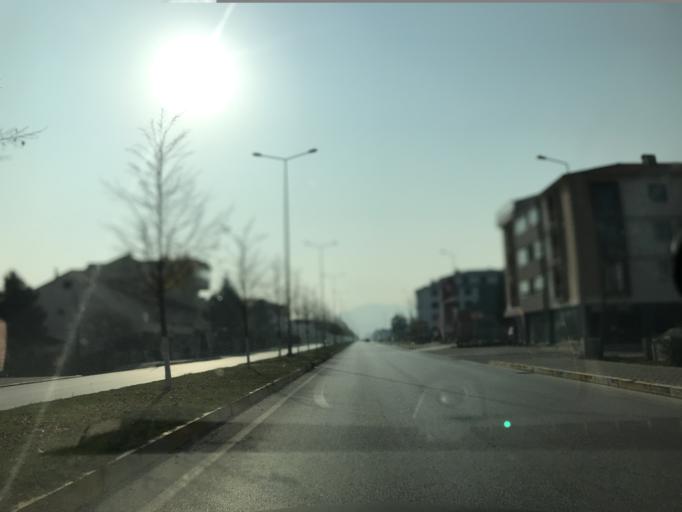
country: TR
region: Duzce
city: Cumayeri
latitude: 40.8687
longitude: 30.9516
